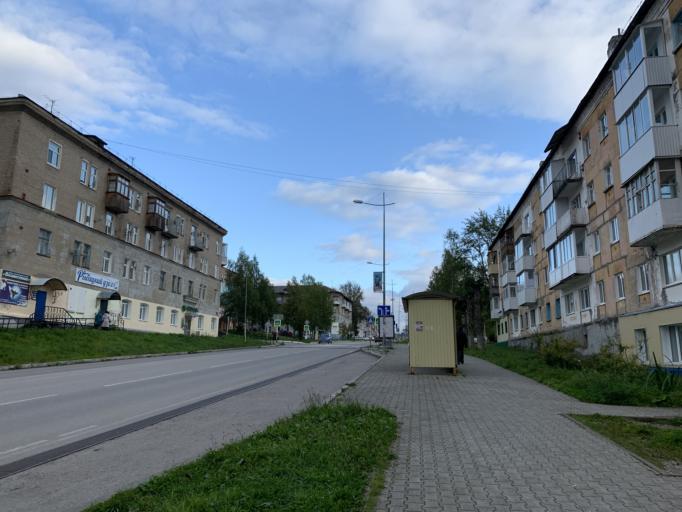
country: RU
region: Perm
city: Gubakha
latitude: 58.8424
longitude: 57.5504
